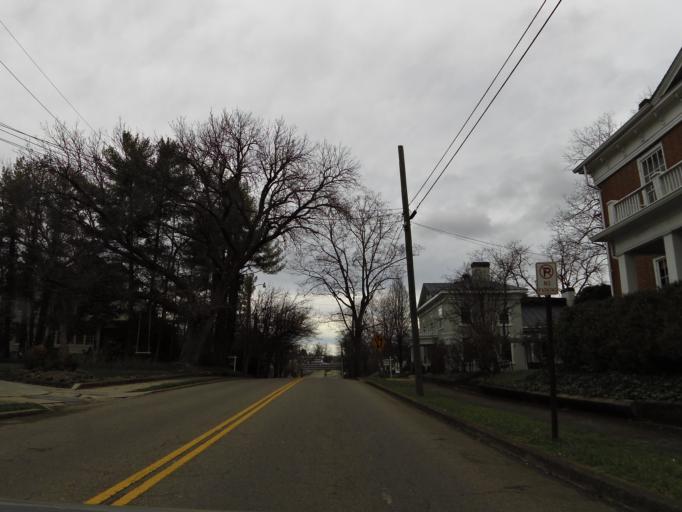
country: US
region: Tennessee
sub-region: Greene County
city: Greeneville
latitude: 36.1682
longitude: -82.8281
